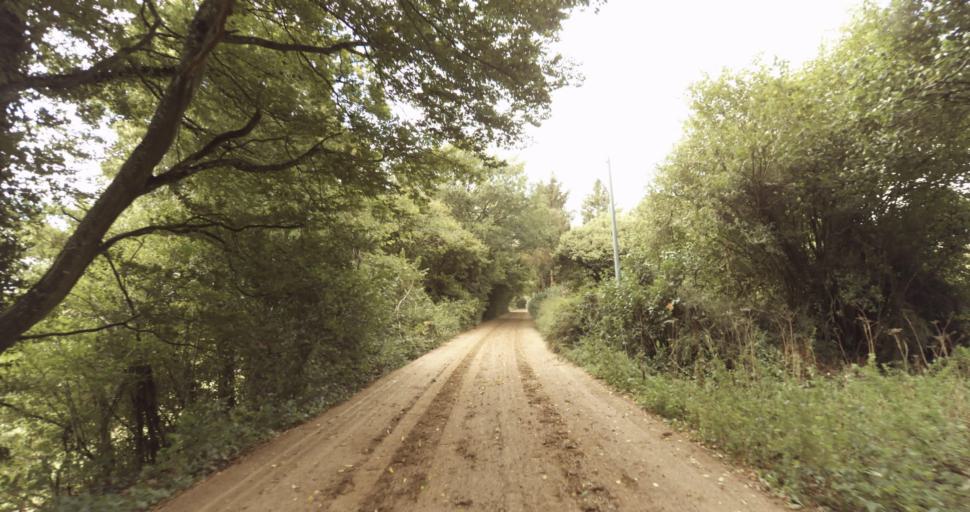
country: FR
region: Lower Normandy
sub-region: Departement de l'Orne
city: Sainte-Gauburge-Sainte-Colombe
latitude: 48.7516
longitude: 0.3716
